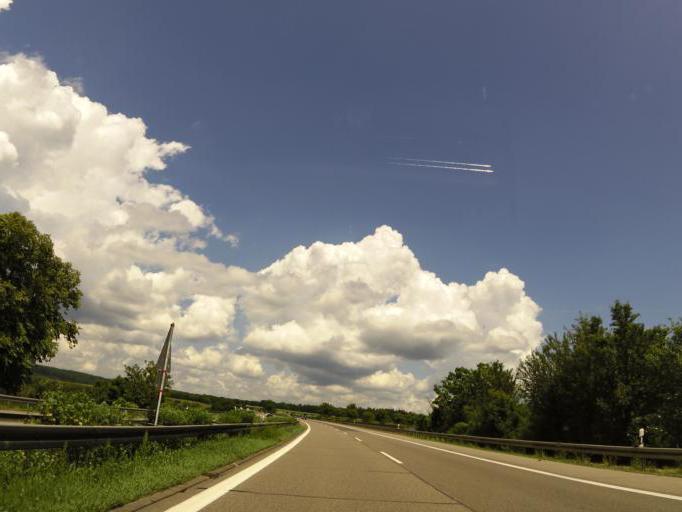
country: DE
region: Baden-Wuerttemberg
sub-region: Regierungsbezirk Stuttgart
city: Giengen an der Brenz
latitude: 48.6240
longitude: 10.2194
